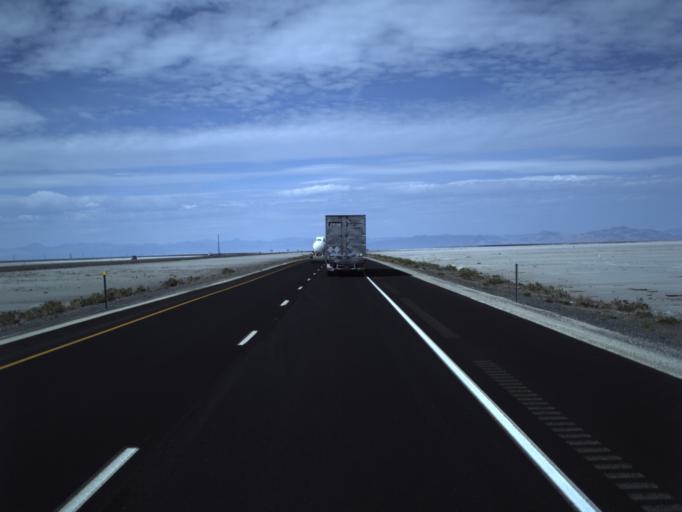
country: US
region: Utah
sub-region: Tooele County
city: Wendover
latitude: 40.7322
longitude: -113.5165
